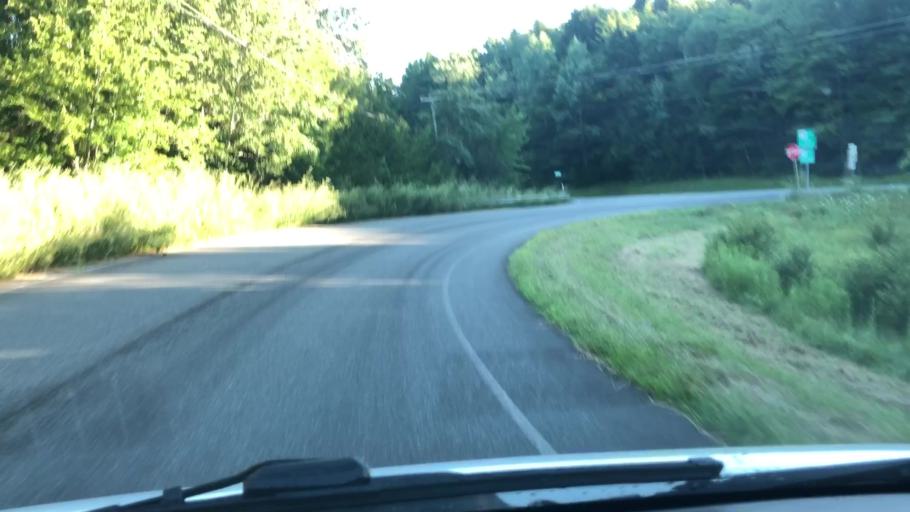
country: US
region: Massachusetts
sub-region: Berkshire County
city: Hinsdale
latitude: 42.4835
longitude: -72.9873
